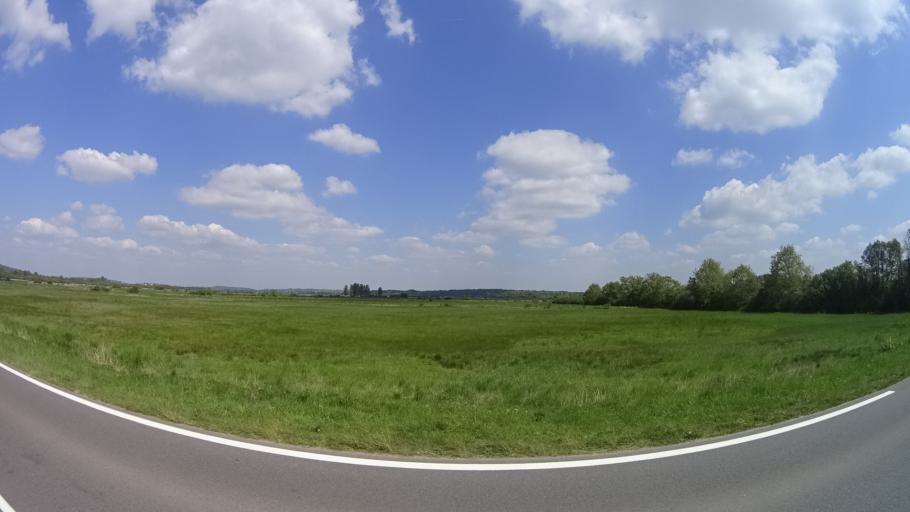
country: FR
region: Brittany
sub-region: Departement du Morbihan
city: Rieux
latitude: 47.6020
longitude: -2.1052
